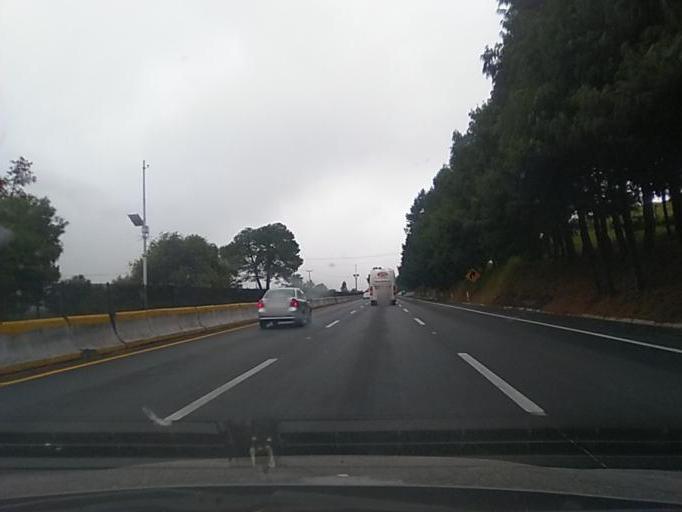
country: MX
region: Mexico City
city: Xochimilco
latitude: 19.1624
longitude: -99.1543
